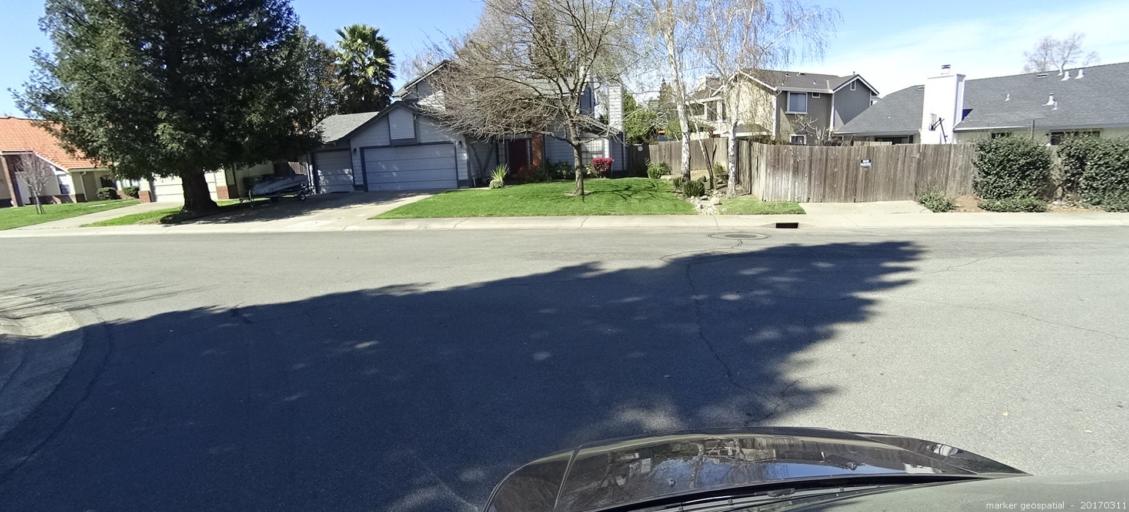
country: US
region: California
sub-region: Sacramento County
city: Parkway
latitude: 38.4824
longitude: -121.5393
